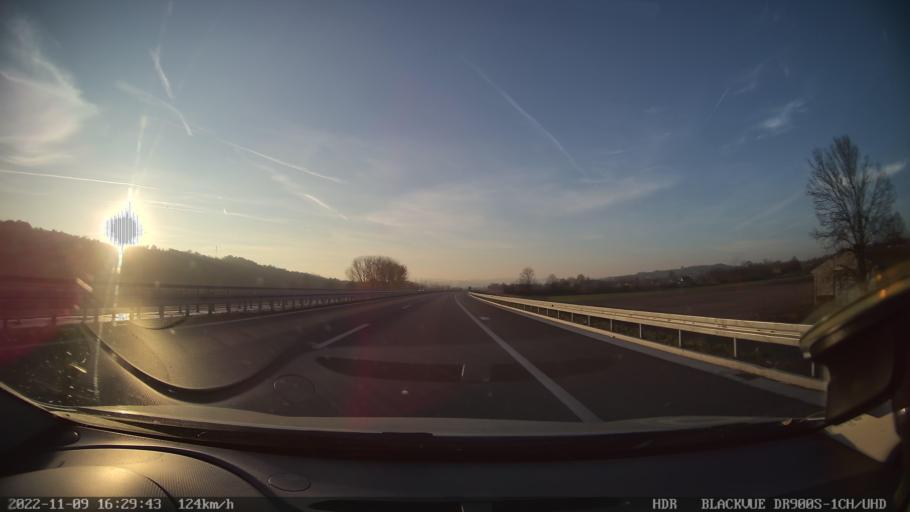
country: RS
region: Central Serbia
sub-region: Moravicki Okrug
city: Cacak
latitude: 43.9250
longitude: 20.3553
